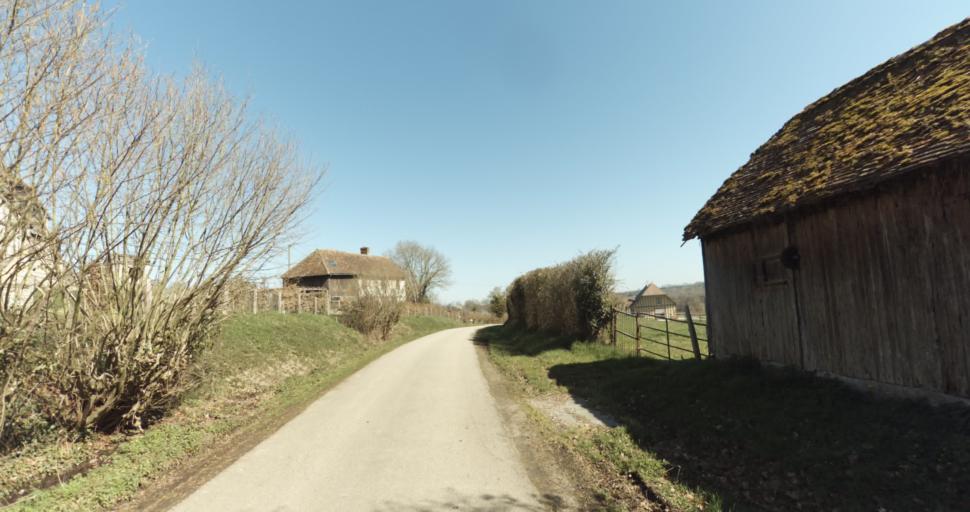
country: FR
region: Lower Normandy
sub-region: Departement du Calvados
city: Livarot
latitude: 48.9900
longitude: 0.0604
